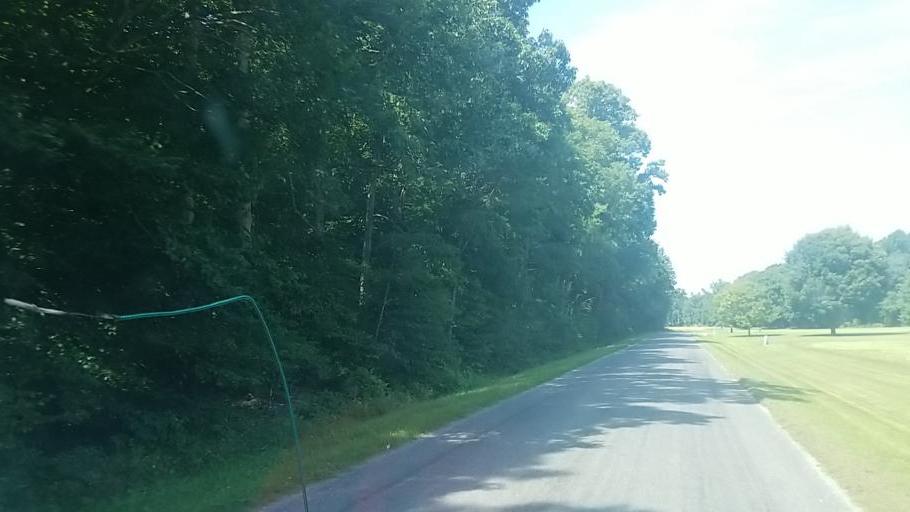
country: US
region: Maryland
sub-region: Caroline County
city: Denton
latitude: 38.8789
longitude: -75.7757
